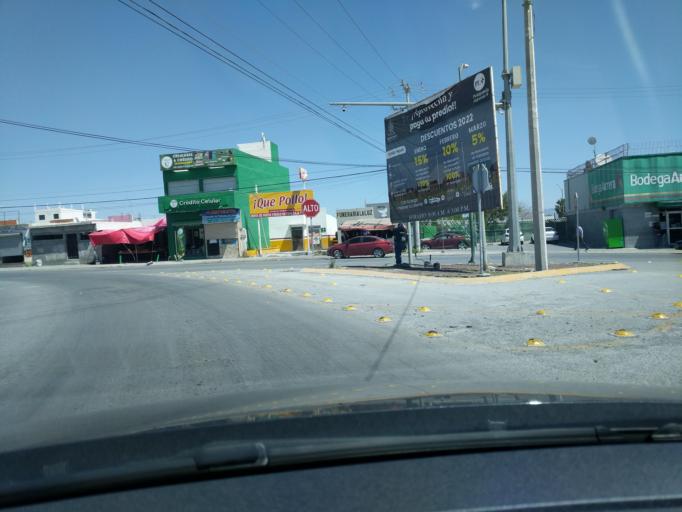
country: MX
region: Nuevo Leon
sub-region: Pesqueria
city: Colinas del Aeropuerto
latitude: 25.8204
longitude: -100.1063
